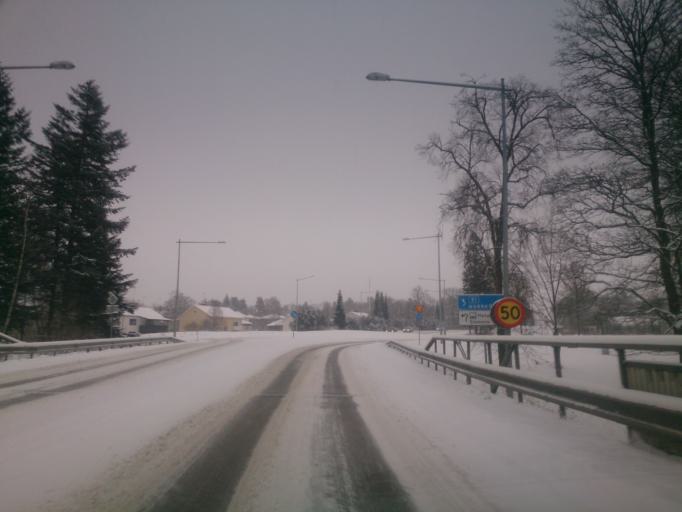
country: SE
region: OEstergoetland
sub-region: Finspangs Kommun
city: Finspang
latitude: 58.7054
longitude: 15.7846
